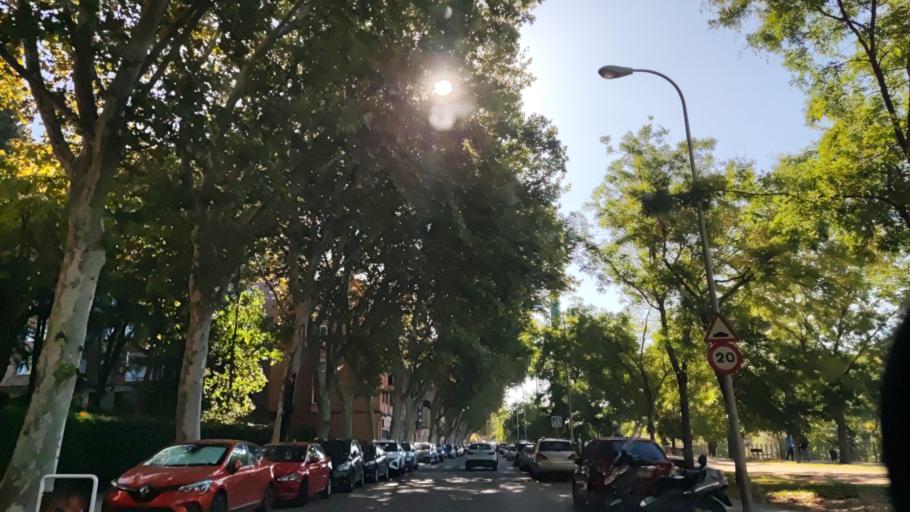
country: ES
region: Madrid
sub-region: Provincia de Madrid
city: Moncloa-Aravaca
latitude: 40.4270
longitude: -3.7290
